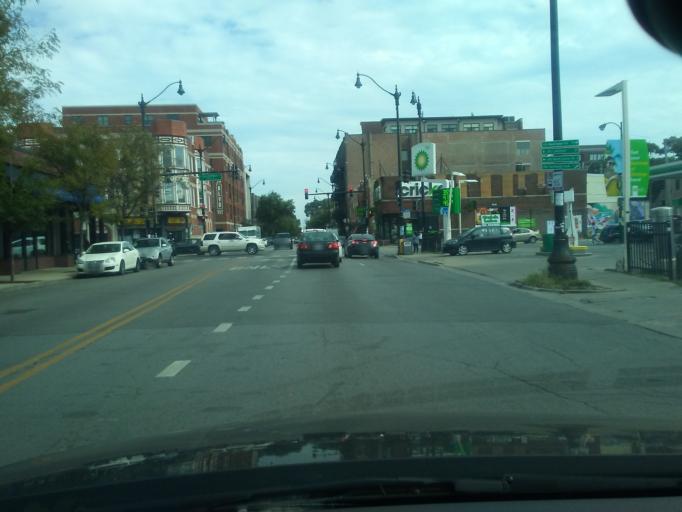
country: US
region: Illinois
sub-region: Cook County
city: Chicago
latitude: 41.9174
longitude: -87.6978
